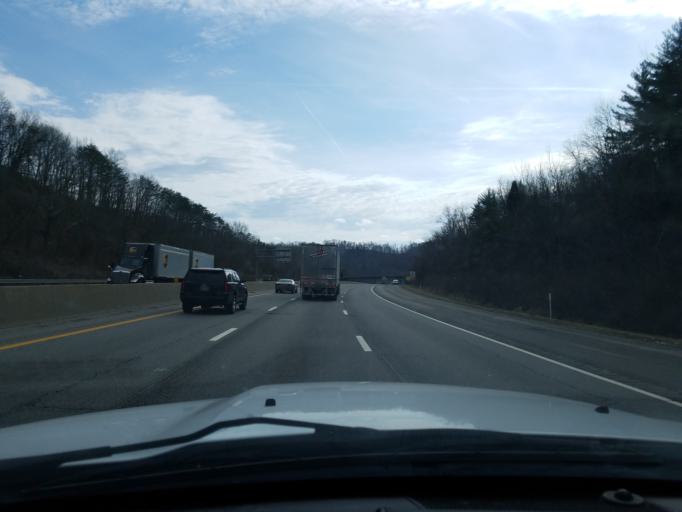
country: US
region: West Virginia
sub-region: Kanawha County
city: Nitro
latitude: 38.4370
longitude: -81.8279
